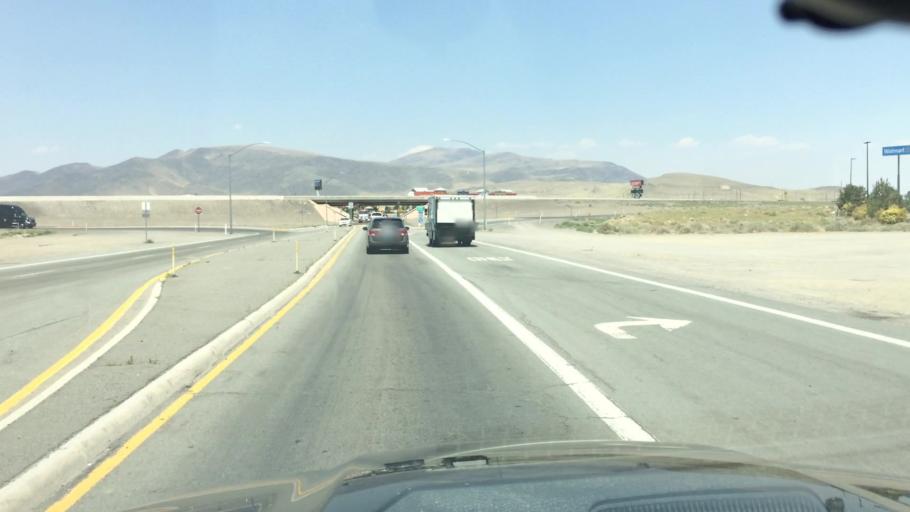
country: US
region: Nevada
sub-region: Lyon County
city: Fernley
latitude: 39.6108
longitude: -119.2190
